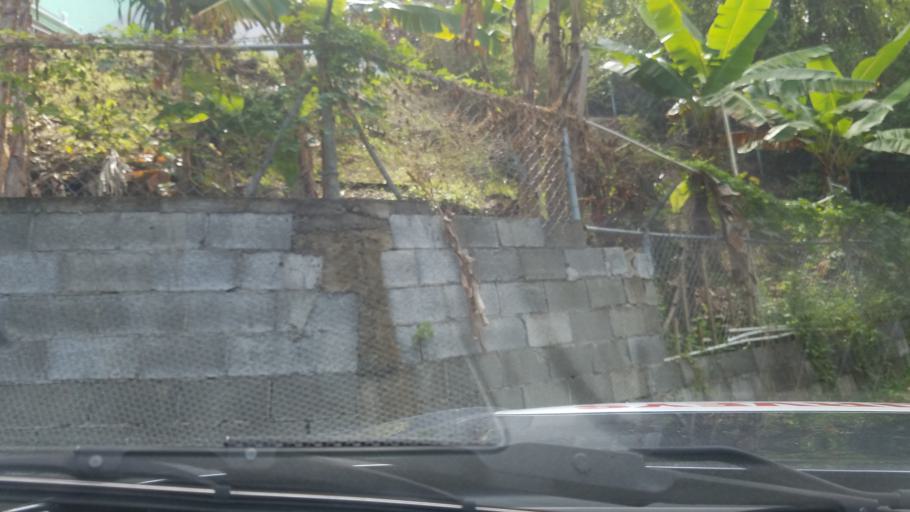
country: LC
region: Castries Quarter
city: Bisee
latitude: 14.0190
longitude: -60.9772
